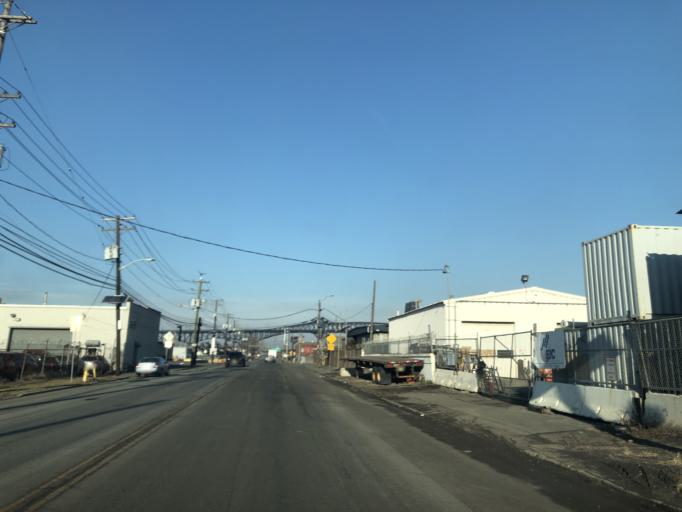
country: US
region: New Jersey
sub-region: Hudson County
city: Harrison
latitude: 40.7276
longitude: -74.1223
